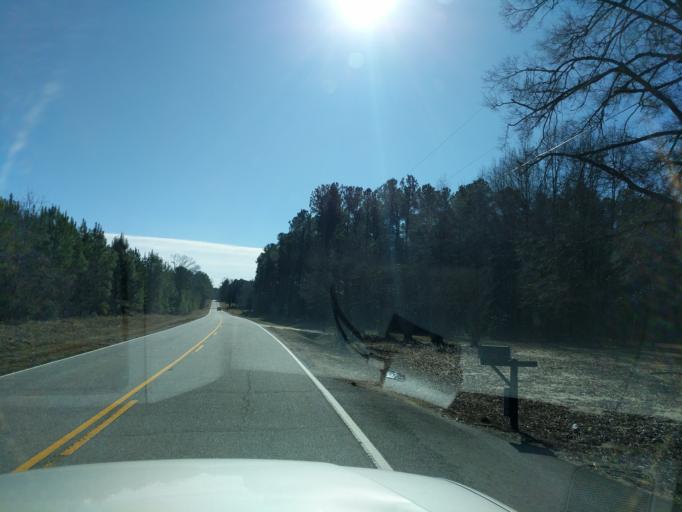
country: US
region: South Carolina
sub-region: Saluda County
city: Saluda
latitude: 34.0928
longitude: -81.8286
